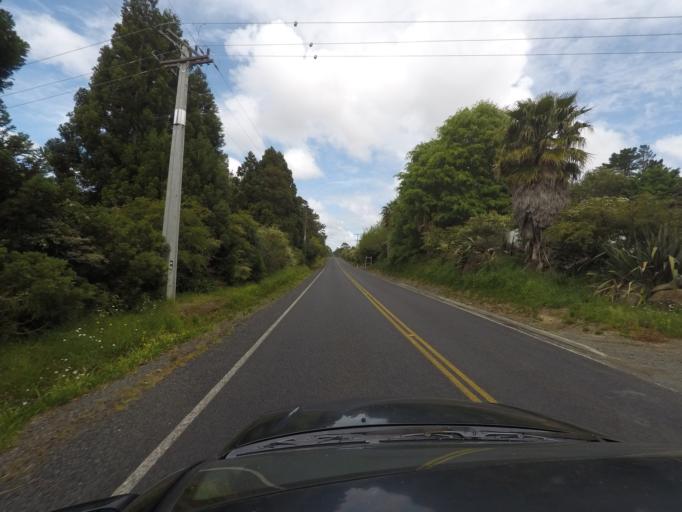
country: NZ
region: Auckland
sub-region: Auckland
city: Parakai
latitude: -36.6435
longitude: 174.5131
